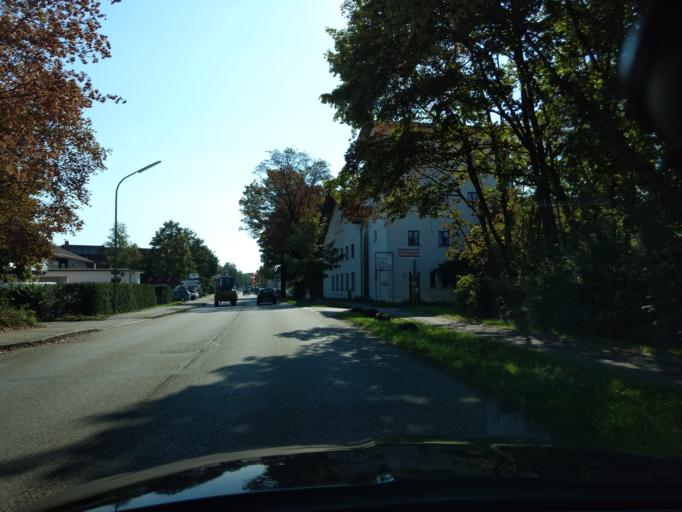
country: DE
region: Bavaria
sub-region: Upper Bavaria
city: Wolfratshausen
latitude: 47.9090
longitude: 11.4258
